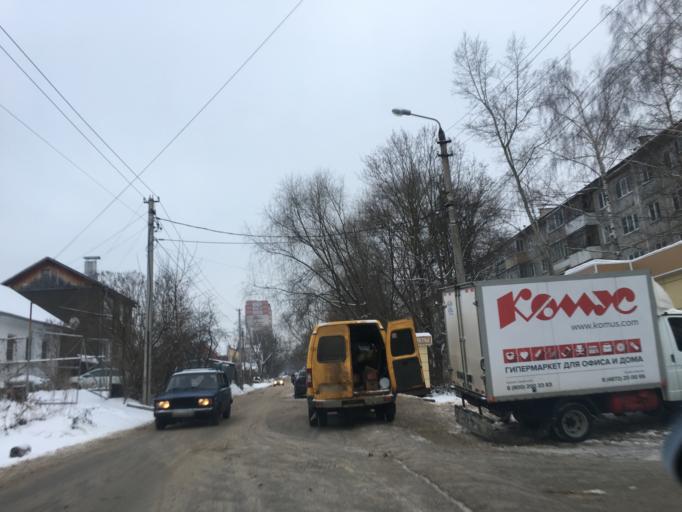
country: RU
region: Tula
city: Mendeleyevskiy
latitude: 54.1813
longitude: 37.5692
